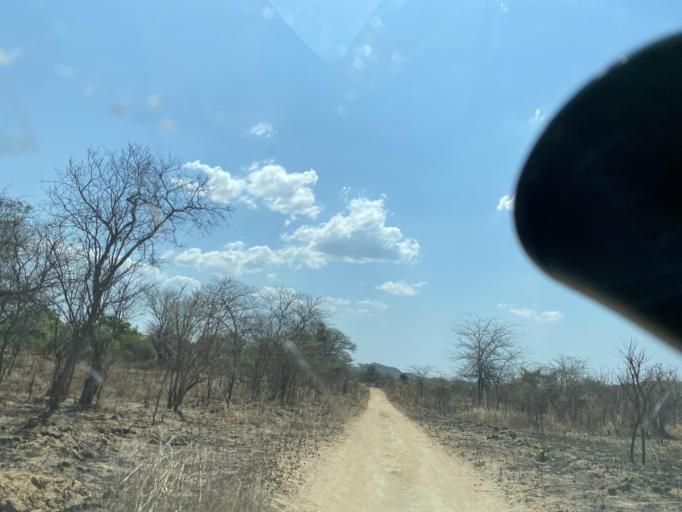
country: ZM
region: Lusaka
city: Chongwe
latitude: -15.0820
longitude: 29.5038
